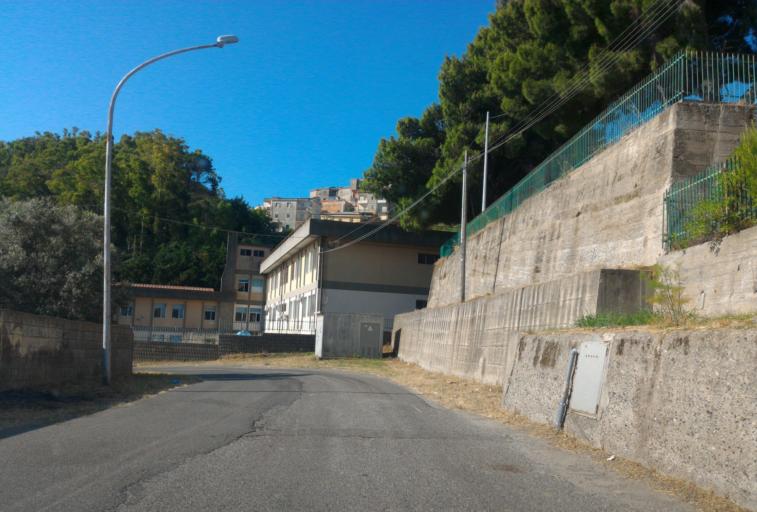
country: IT
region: Calabria
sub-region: Provincia di Crotone
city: Ciro
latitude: 39.3825
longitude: 17.0672
